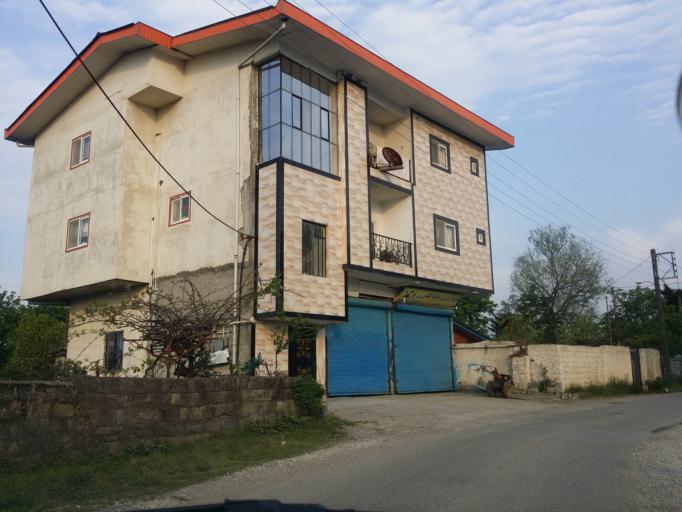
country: IR
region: Mazandaran
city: Chalus
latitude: 36.6660
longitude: 51.3681
